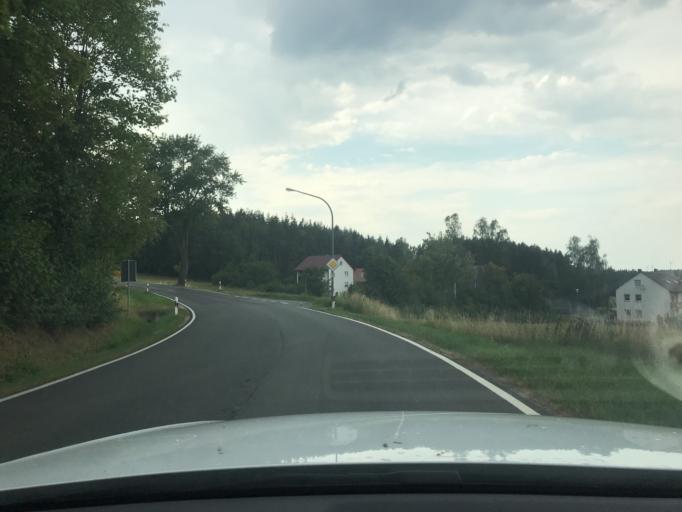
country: DE
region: Bavaria
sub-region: Upper Franconia
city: Prebitz
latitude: 49.7939
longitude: 11.6769
